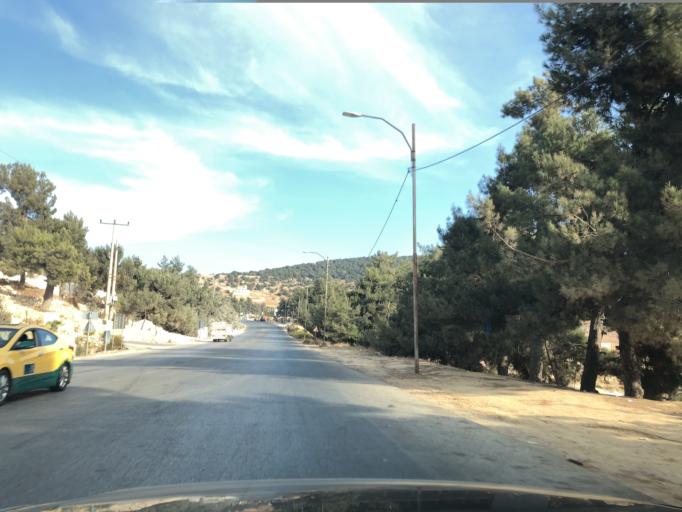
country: JO
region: Irbid
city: `Anjarah
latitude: 32.3141
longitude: 35.7730
